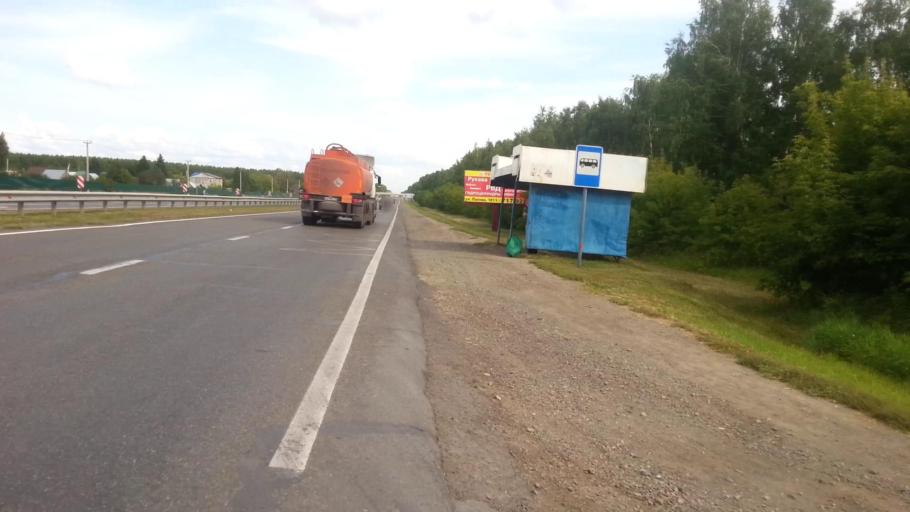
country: RU
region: Altai Krai
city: Vlasikha
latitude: 53.3543
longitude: 83.5411
